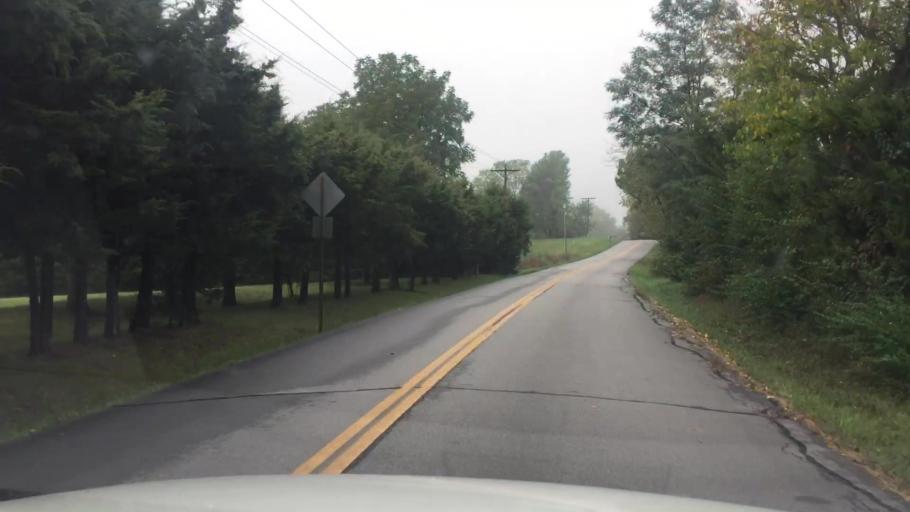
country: US
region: Missouri
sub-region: Boone County
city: Ashland
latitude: 38.8560
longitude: -92.3065
